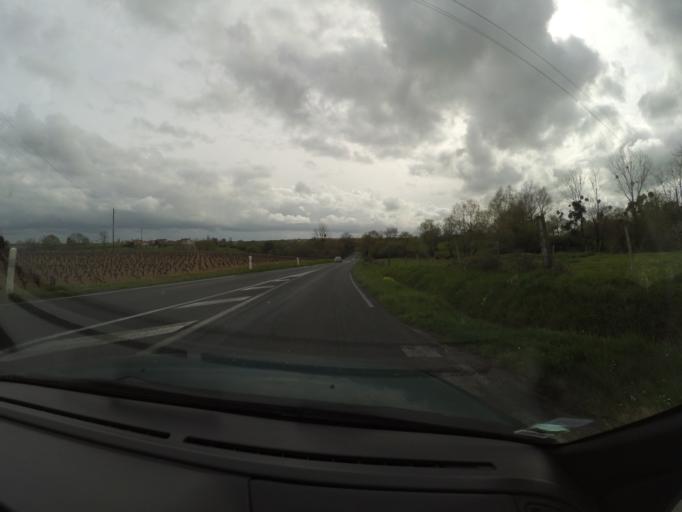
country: FR
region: Pays de la Loire
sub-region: Departement de Maine-et-Loire
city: Lire
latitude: 47.3080
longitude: -1.1614
